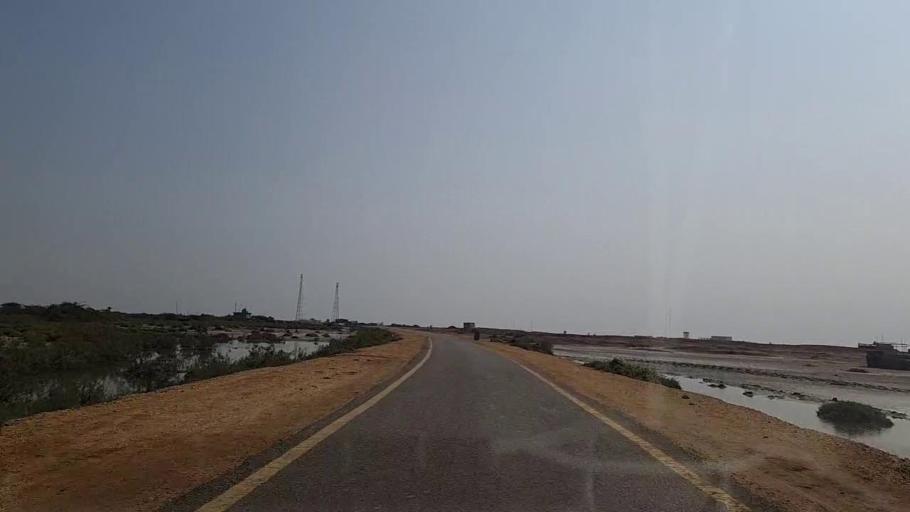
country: PK
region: Sindh
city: Chuhar Jamali
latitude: 24.1697
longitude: 67.8946
